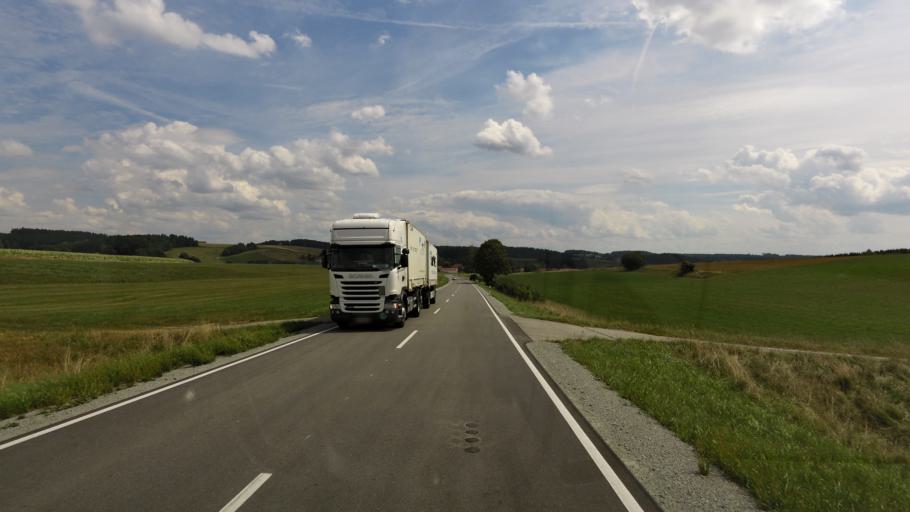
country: DE
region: Bavaria
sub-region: Upper Bavaria
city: Niedertaufkirchen
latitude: 48.3201
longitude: 12.5472
